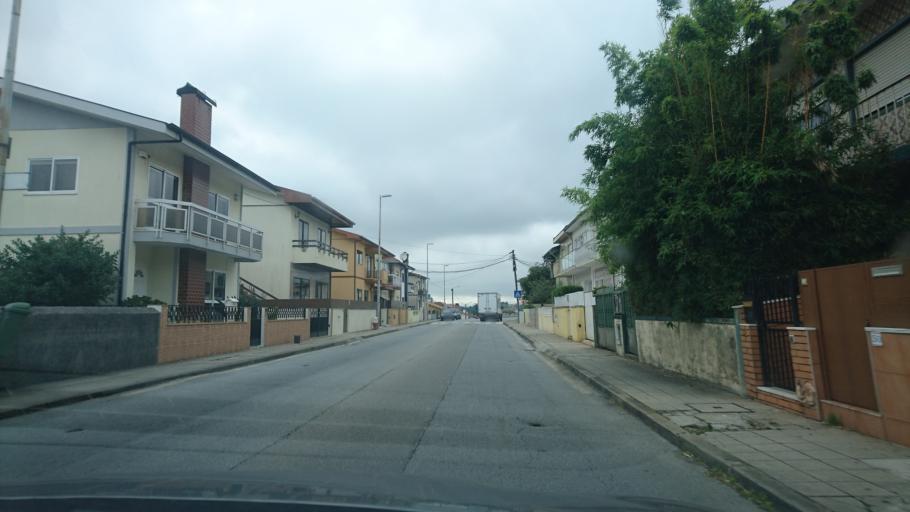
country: PT
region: Porto
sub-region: Valongo
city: Valongo
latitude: 41.1918
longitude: -8.5102
